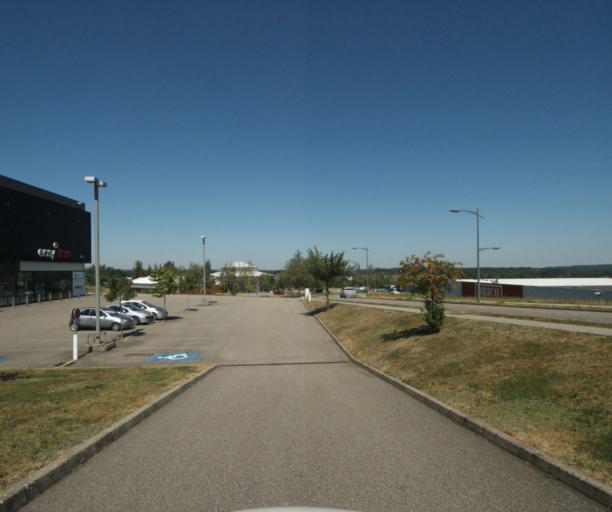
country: FR
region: Lorraine
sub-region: Departement des Vosges
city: Epinal
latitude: 48.1881
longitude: 6.4709
